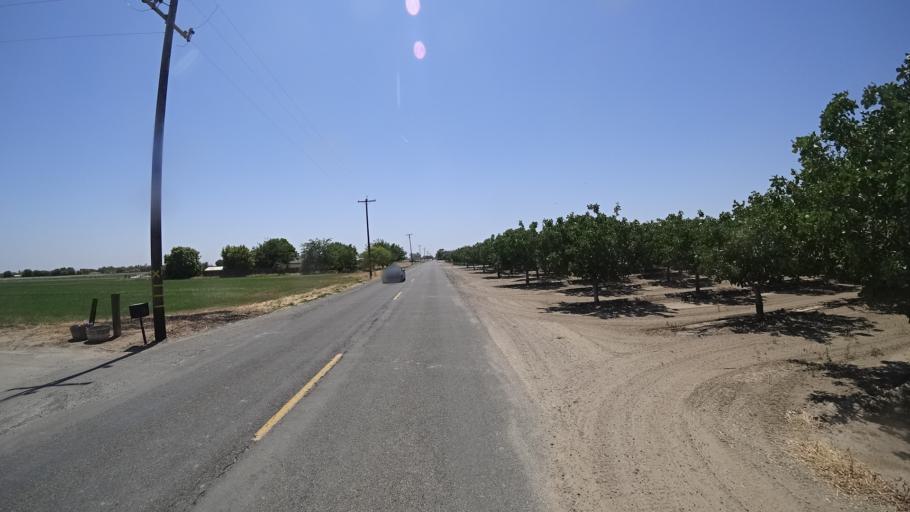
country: US
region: California
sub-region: Kings County
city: Lemoore
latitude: 36.2605
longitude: -119.7630
